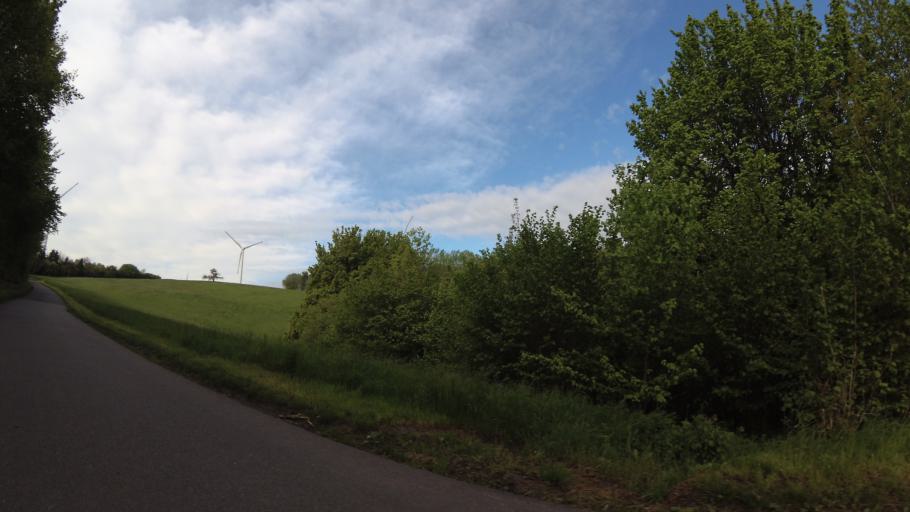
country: DE
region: Saarland
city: Orscholz
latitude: 49.4400
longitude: 6.5461
